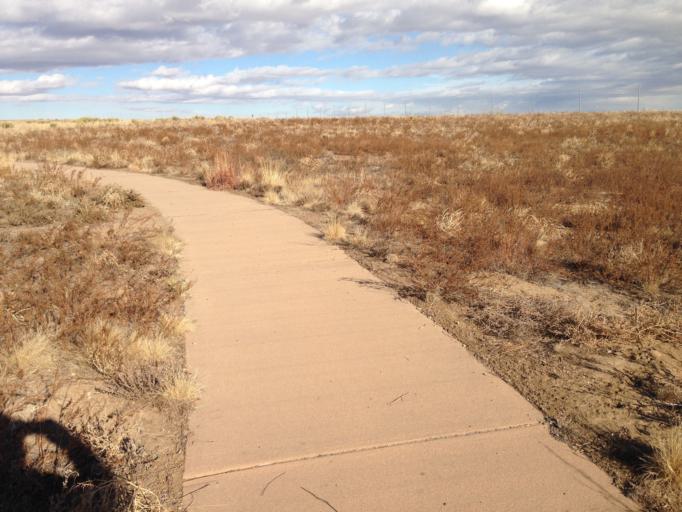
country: US
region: Colorado
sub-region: Adams County
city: Derby
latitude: 39.8328
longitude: -104.8546
